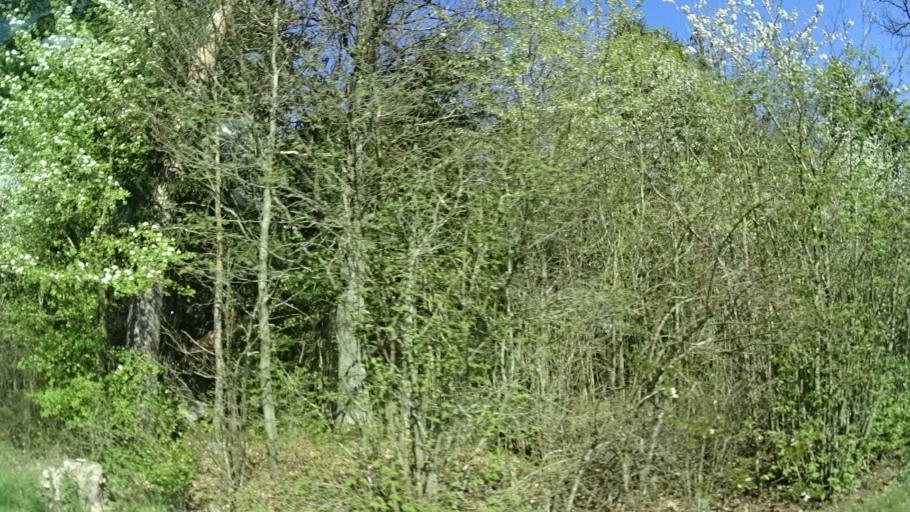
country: DE
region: Bavaria
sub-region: Upper Palatinate
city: Edelsfeld
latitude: 49.5498
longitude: 11.7144
